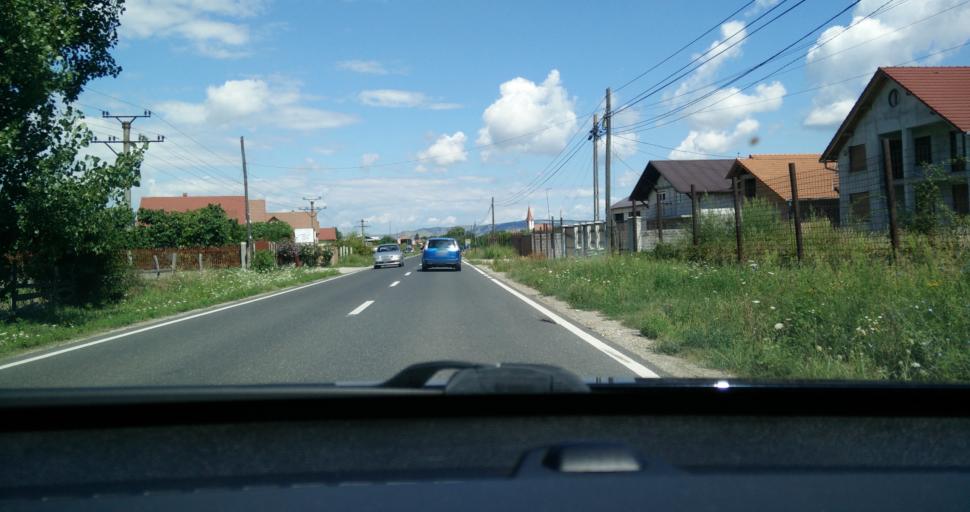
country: RO
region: Alba
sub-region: Municipiul Sebes
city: Petresti
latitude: 45.9138
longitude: 23.5547
